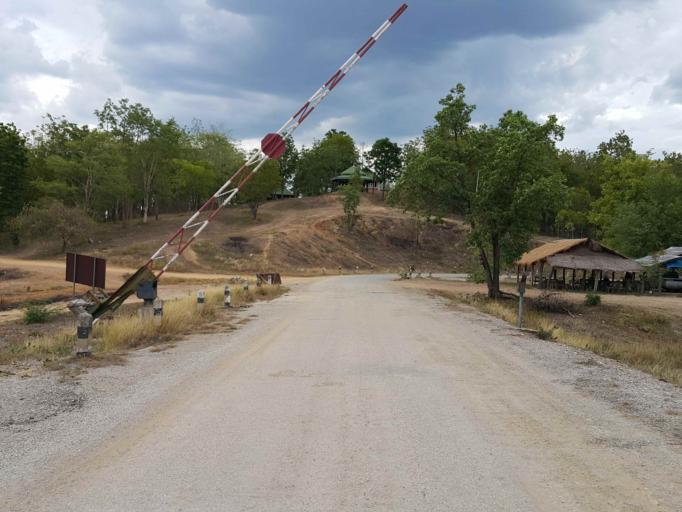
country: TH
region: Sukhothai
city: Thung Saliam
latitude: 17.3271
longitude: 99.4218
